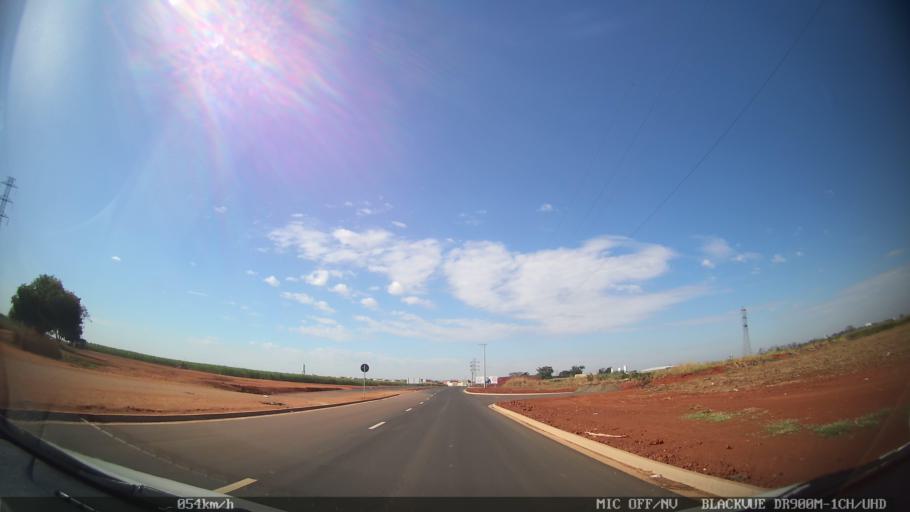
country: BR
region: Sao Paulo
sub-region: Santa Barbara D'Oeste
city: Santa Barbara d'Oeste
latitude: -22.7247
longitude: -47.4106
